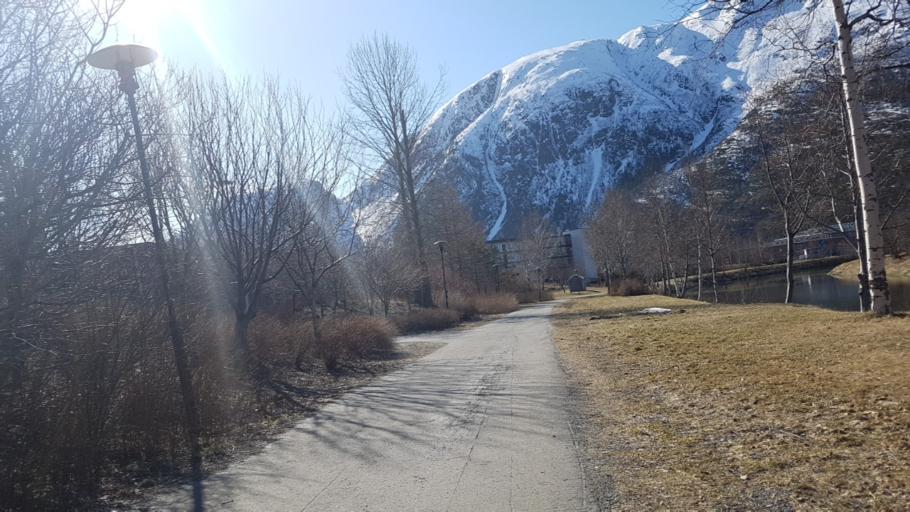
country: NO
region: Nordland
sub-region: Vefsn
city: Mosjoen
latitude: 65.8419
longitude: 13.2004
